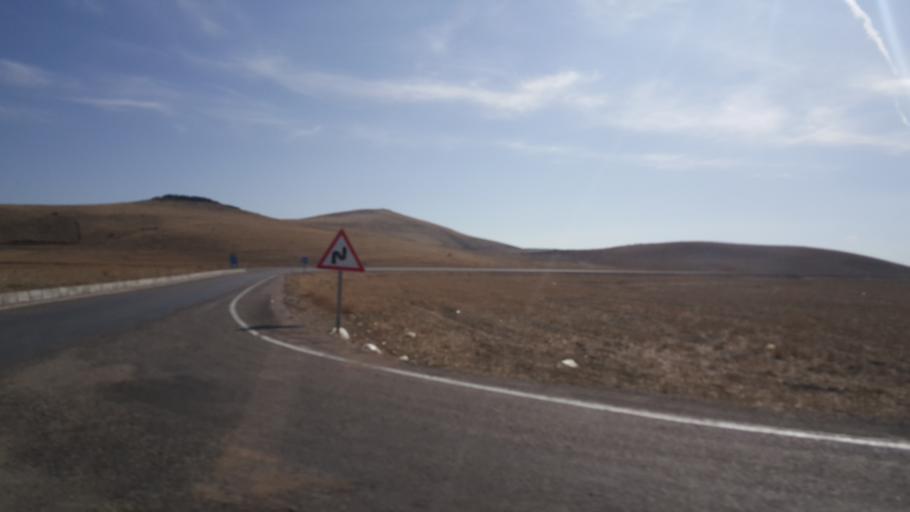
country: TR
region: Ankara
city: Yenice
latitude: 39.3830
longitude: 32.8218
